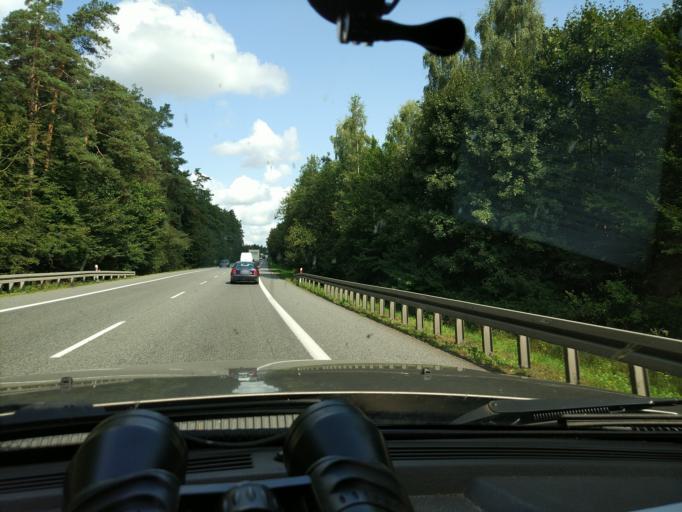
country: PL
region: Masovian Voivodeship
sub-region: Powiat mlawski
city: Mlawa
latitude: 53.1358
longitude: 20.3964
